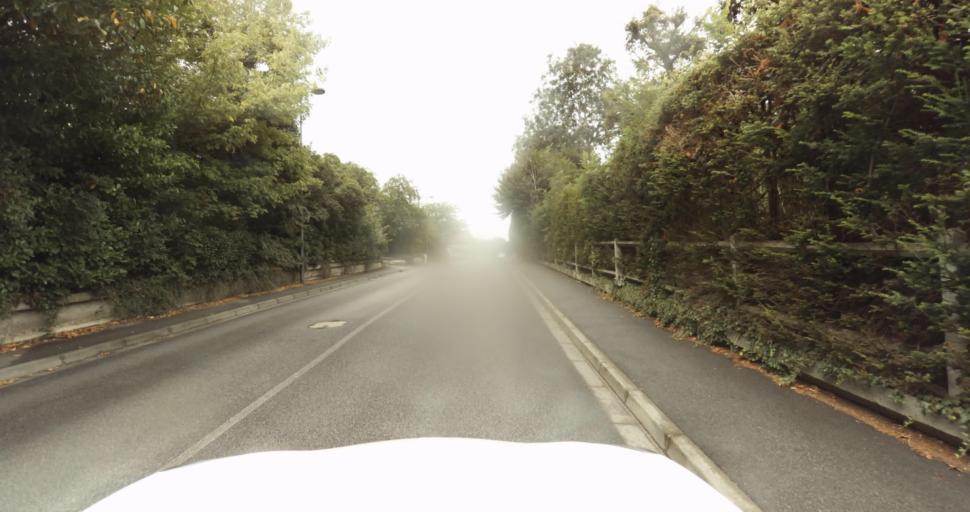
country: FR
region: Haute-Normandie
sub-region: Departement de l'Eure
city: Evreux
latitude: 49.0282
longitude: 1.1372
